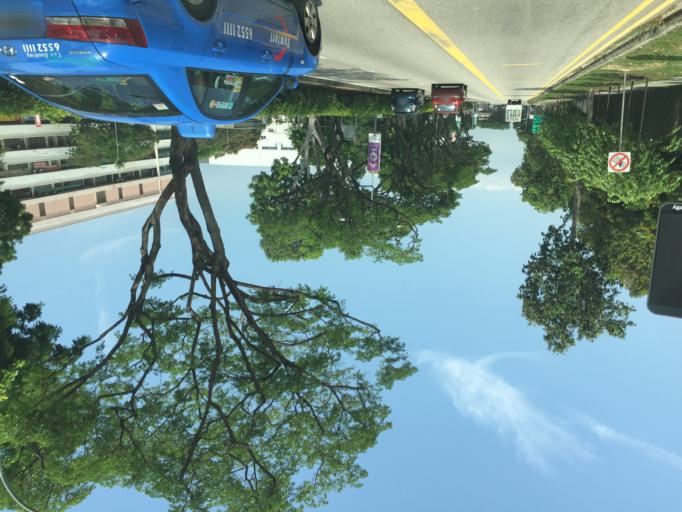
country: SG
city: Singapore
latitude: 1.3370
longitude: 103.9509
